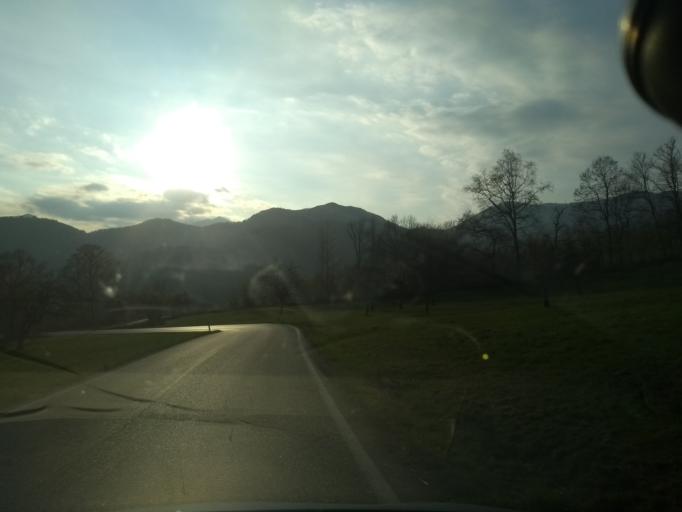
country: IT
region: Piedmont
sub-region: Provincia di Torino
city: Lanzo Torinese
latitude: 45.2889
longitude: 7.4791
